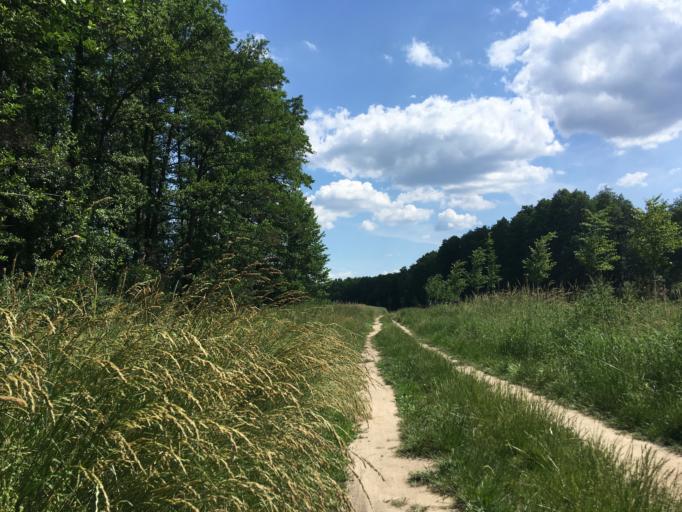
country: DE
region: Brandenburg
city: Hoppegarten
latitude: 52.5416
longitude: 13.6666
